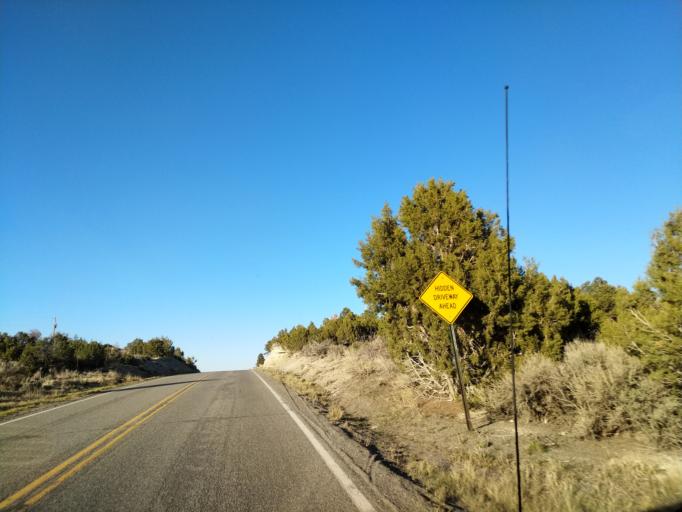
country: US
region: Colorado
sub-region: Mesa County
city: Redlands
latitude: 38.9977
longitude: -108.7139
